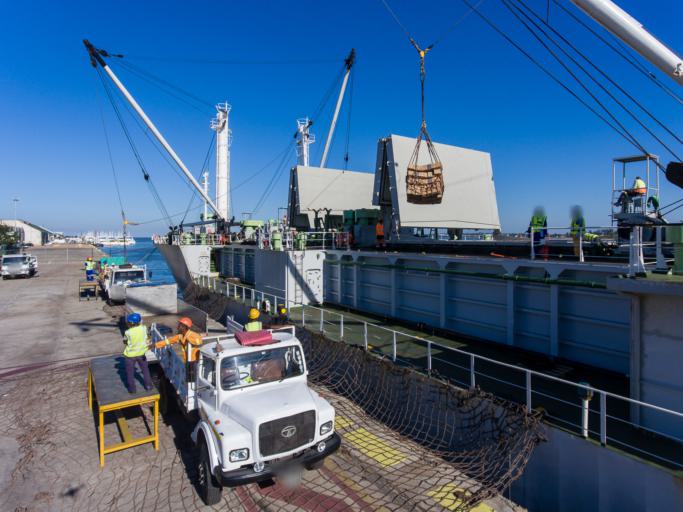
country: MZ
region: Maputo City
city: Maputo
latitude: -25.9722
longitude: 32.5621
